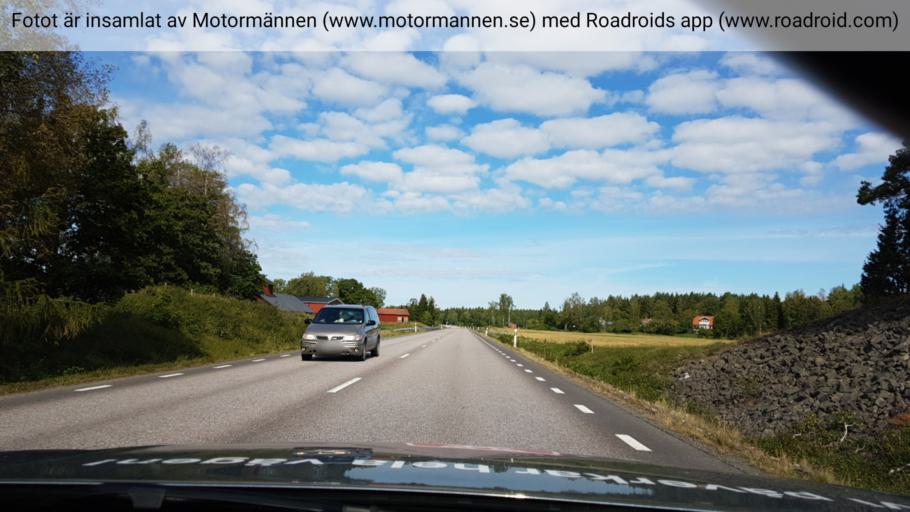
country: SE
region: Uppsala
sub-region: Osthammars Kommun
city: Bjorklinge
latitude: 59.9538
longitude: 17.4051
